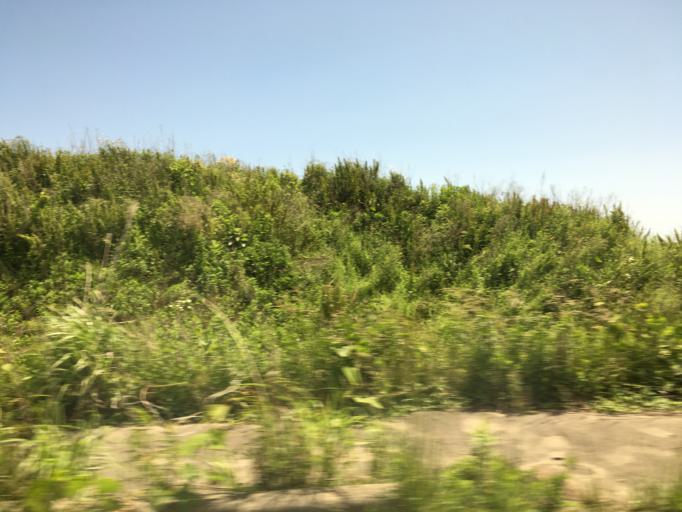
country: JP
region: Fukushima
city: Namie
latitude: 37.4739
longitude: 141.0299
